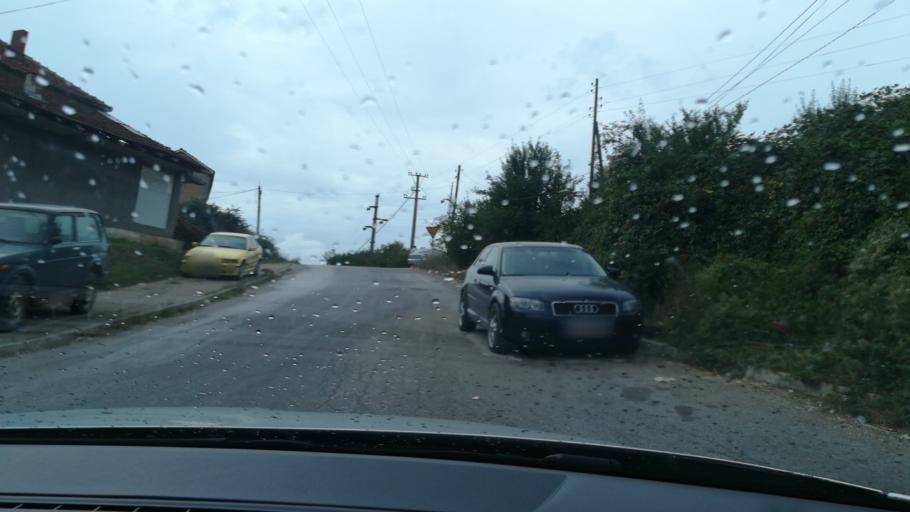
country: MK
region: Kicevo
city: Kicevo
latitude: 41.5095
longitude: 20.9477
